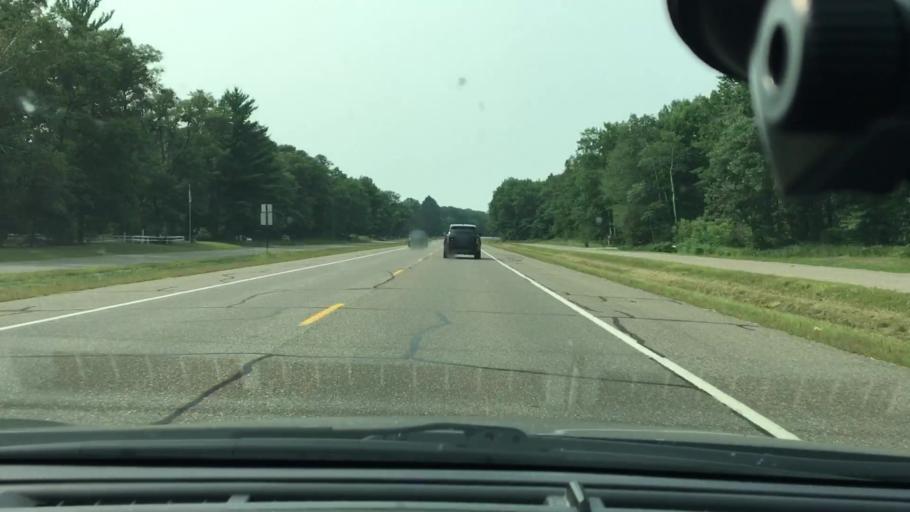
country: US
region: Minnesota
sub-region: Crow Wing County
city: Breezy Point
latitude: 46.4985
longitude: -94.1449
